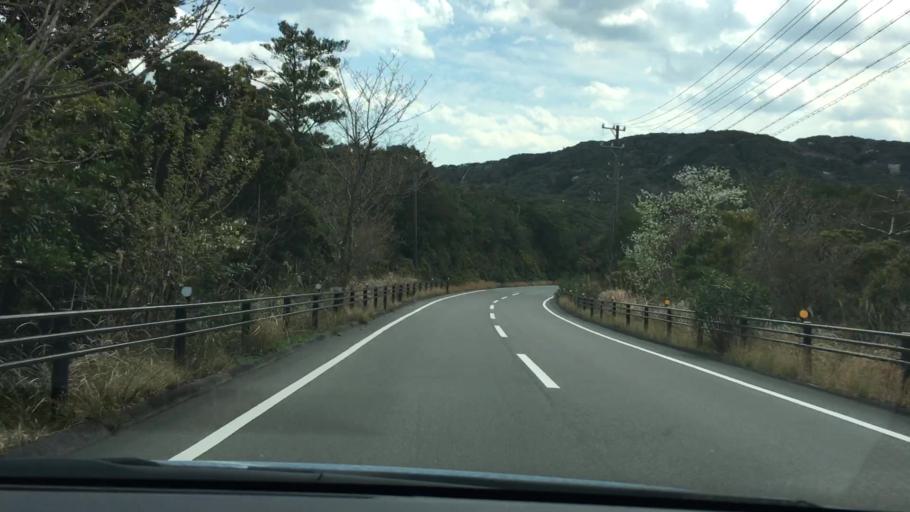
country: JP
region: Mie
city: Toba
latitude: 34.4468
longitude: 136.9047
